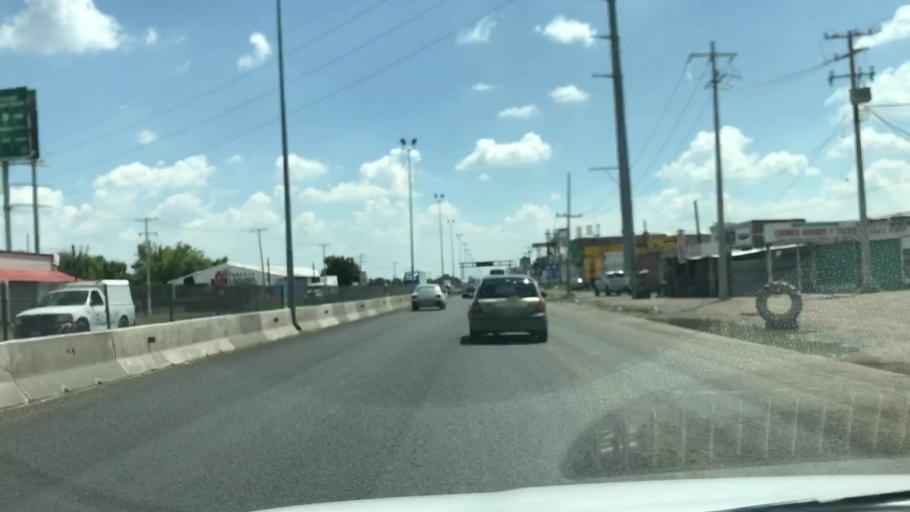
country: MX
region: Guanajuato
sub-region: Irapuato
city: Las Huertas Tercera Seccion
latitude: 20.6473
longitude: -101.3757
